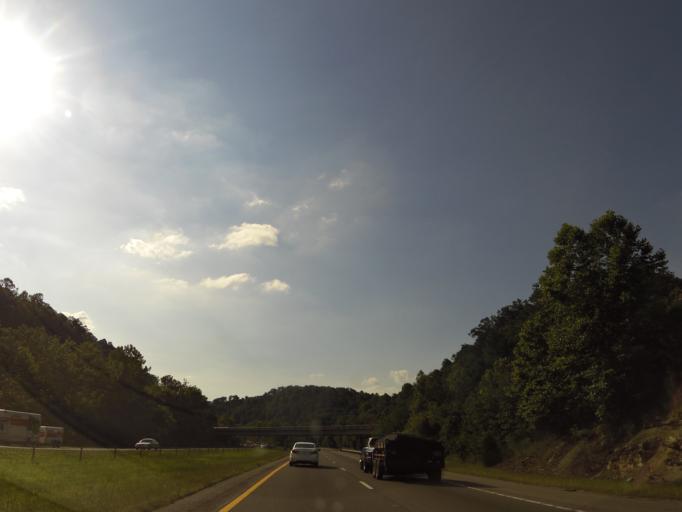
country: US
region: Tennessee
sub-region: Robertson County
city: Ridgetop
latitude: 36.3151
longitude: -86.8326
